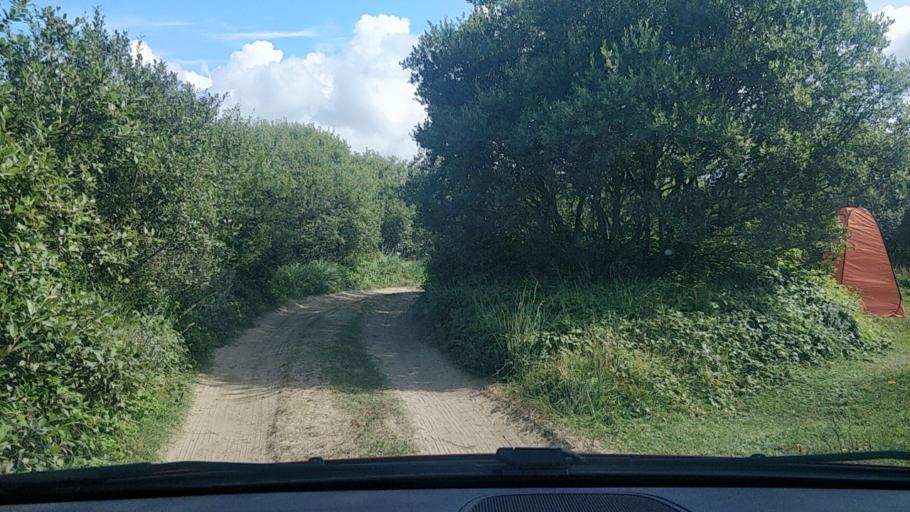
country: GB
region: Wales
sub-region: Gwynedd
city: Llanfair
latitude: 52.8104
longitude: -4.1453
